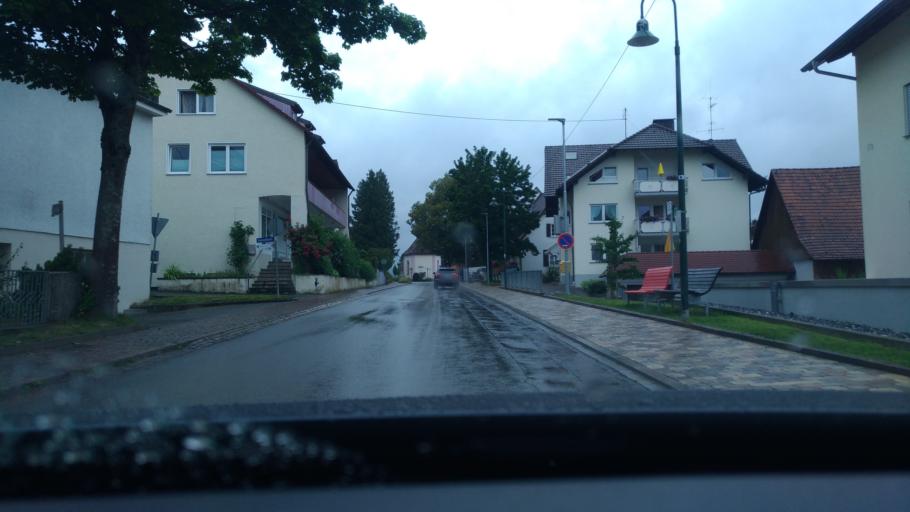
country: DE
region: Baden-Wuerttemberg
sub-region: Freiburg Region
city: Bodman-Ludwigshafen
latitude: 47.8022
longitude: 9.0313
